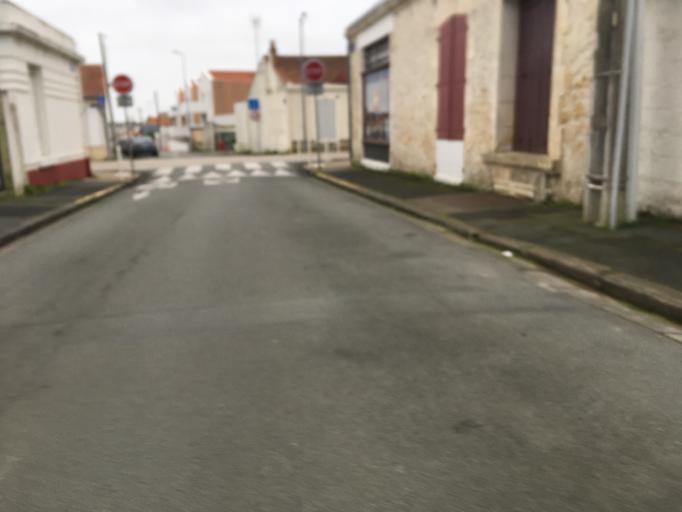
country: FR
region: Poitou-Charentes
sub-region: Departement de la Charente-Maritime
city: La Rochelle
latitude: 46.1700
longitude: -1.1589
